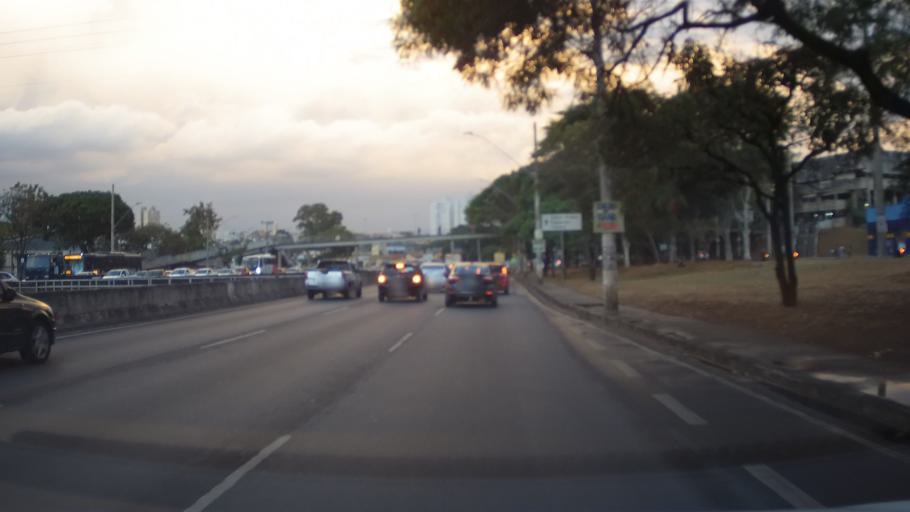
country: BR
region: Minas Gerais
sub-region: Belo Horizonte
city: Belo Horizonte
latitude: -19.9224
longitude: -43.9721
